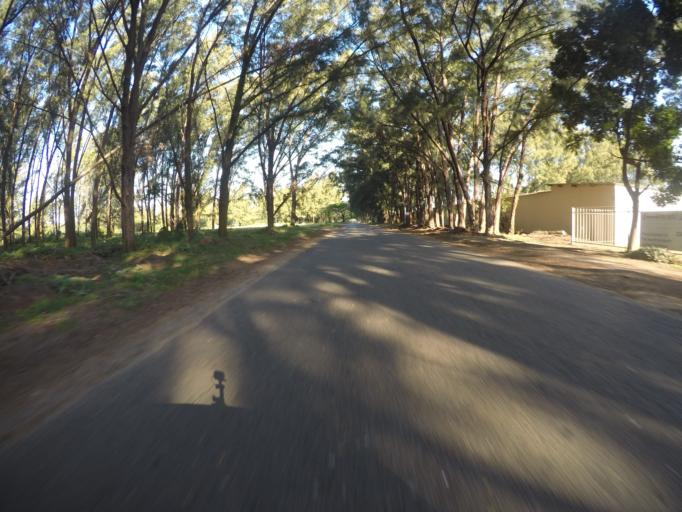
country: ZA
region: KwaZulu-Natal
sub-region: uThungulu District Municipality
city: Richards Bay
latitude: -28.7897
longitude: 32.0839
